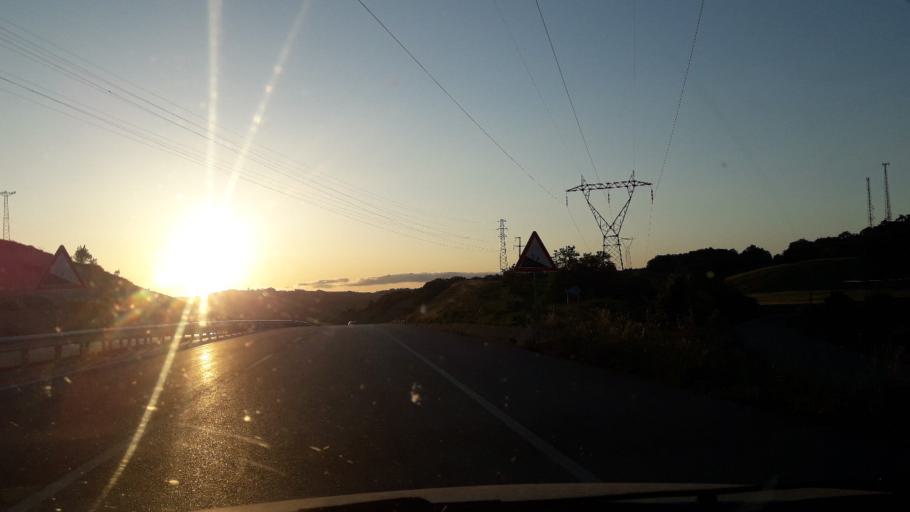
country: TR
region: Sinop
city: Kabali
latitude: 41.8527
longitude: 35.1190
